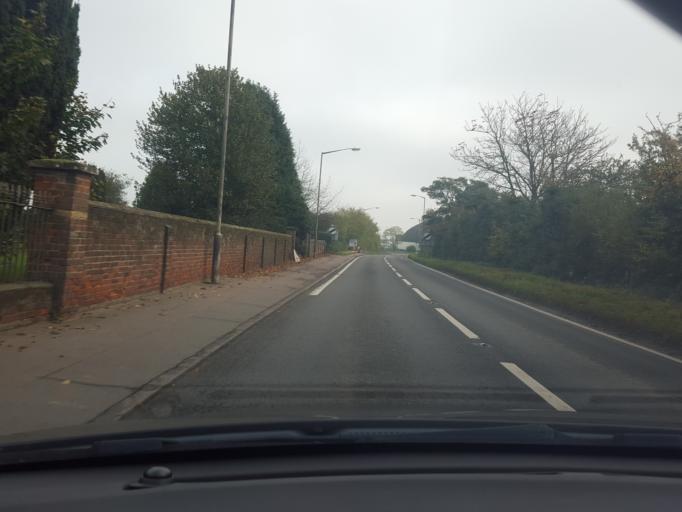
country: GB
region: England
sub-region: Suffolk
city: East Bergholt
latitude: 51.9264
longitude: 0.9883
